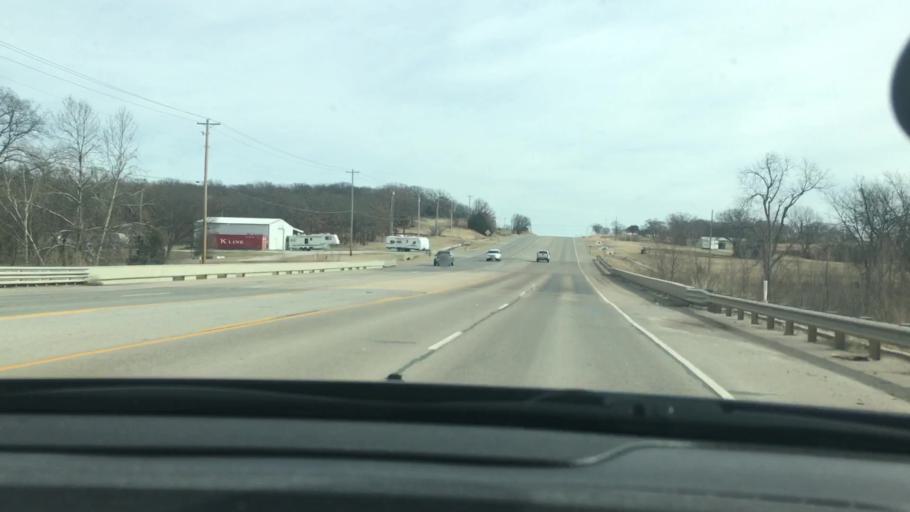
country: US
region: Oklahoma
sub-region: Carter County
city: Dickson
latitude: 34.1871
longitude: -97.0310
